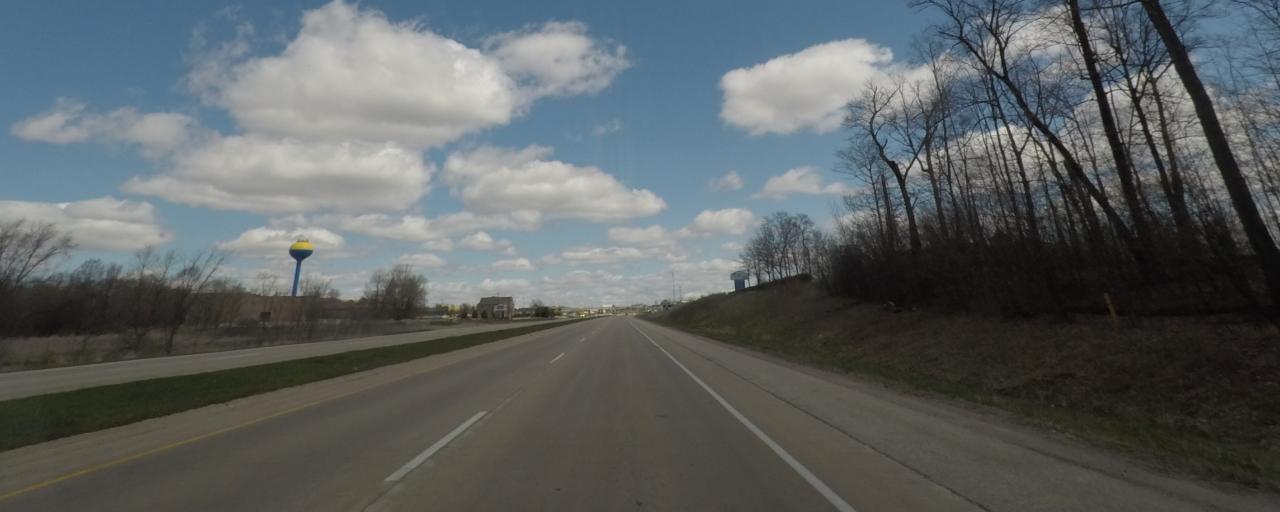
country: US
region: Wisconsin
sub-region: Jefferson County
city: Johnson Creek
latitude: 43.0780
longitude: -88.7660
